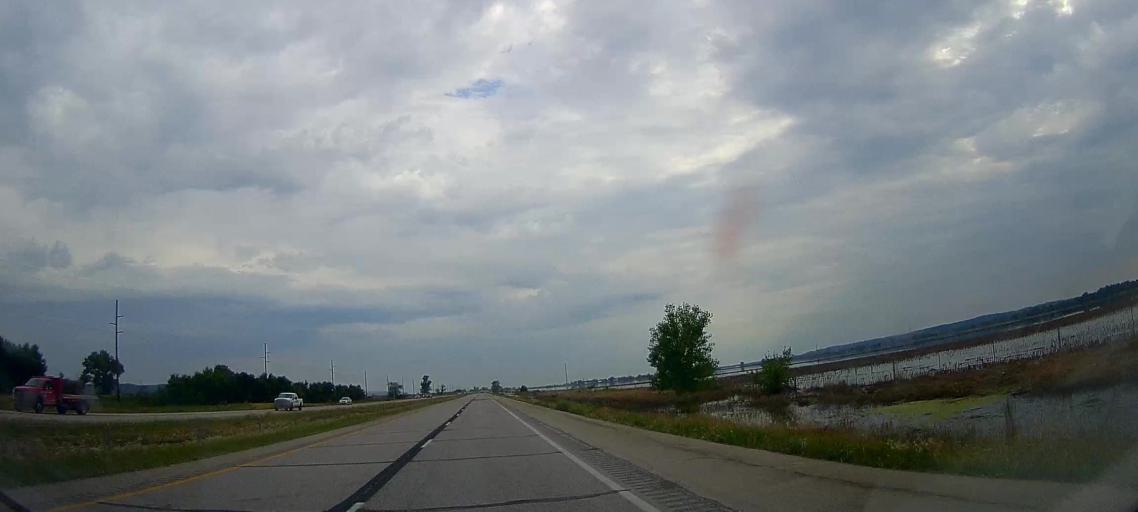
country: US
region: Iowa
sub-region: Harrison County
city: Missouri Valley
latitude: 41.4511
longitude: -95.8998
